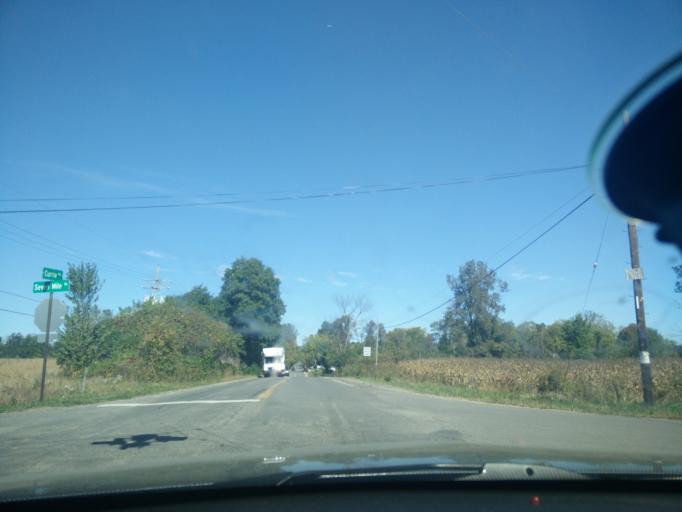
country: US
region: Michigan
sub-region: Oakland County
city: South Lyon
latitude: 42.4195
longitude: -83.5894
